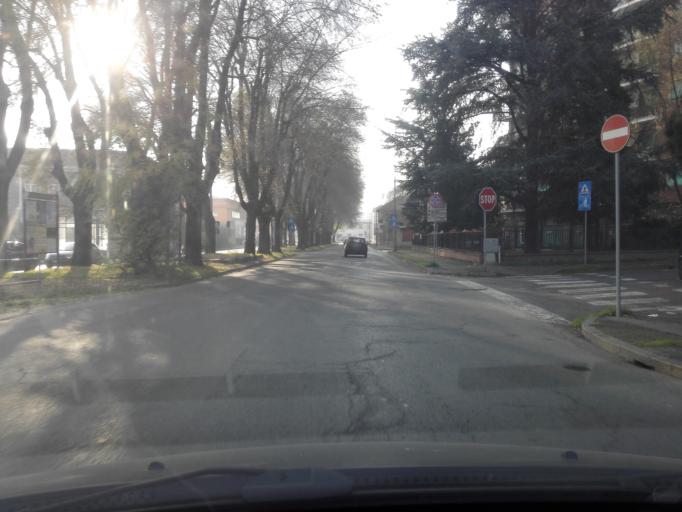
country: IT
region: Piedmont
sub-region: Provincia di Alessandria
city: Alessandria
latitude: 44.9096
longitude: 8.6305
